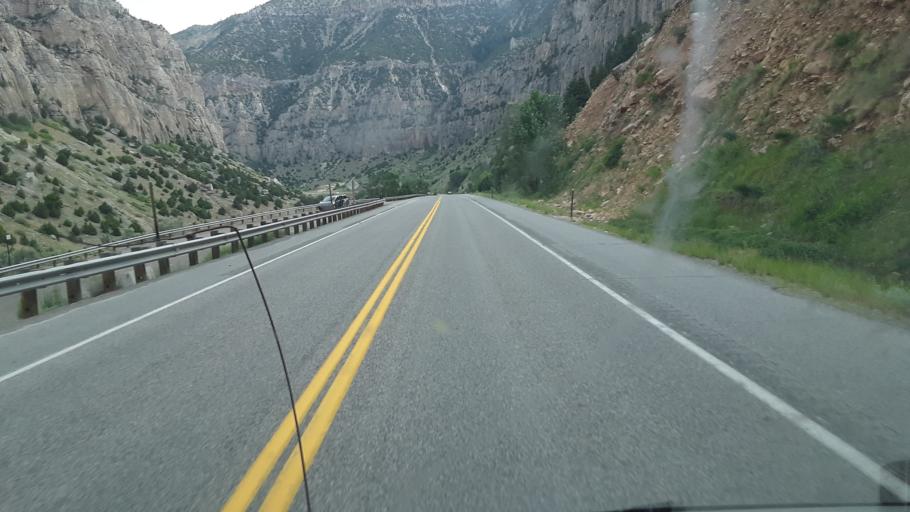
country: US
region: Wyoming
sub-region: Hot Springs County
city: Thermopolis
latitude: 43.5184
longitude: -108.1818
